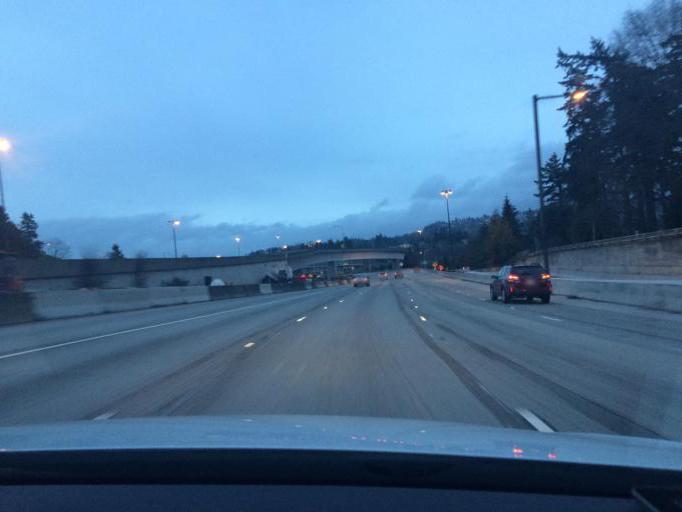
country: US
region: Washington
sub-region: King County
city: Newport
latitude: 47.5797
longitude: -122.1942
